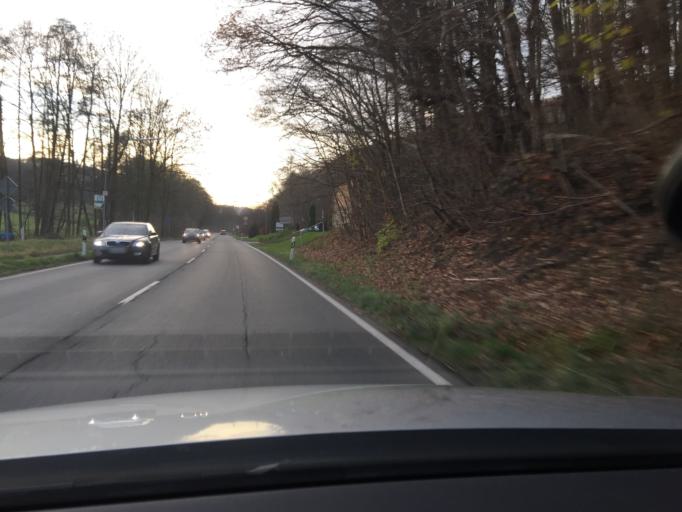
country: DE
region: North Rhine-Westphalia
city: Hattingen
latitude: 51.3720
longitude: 7.1763
